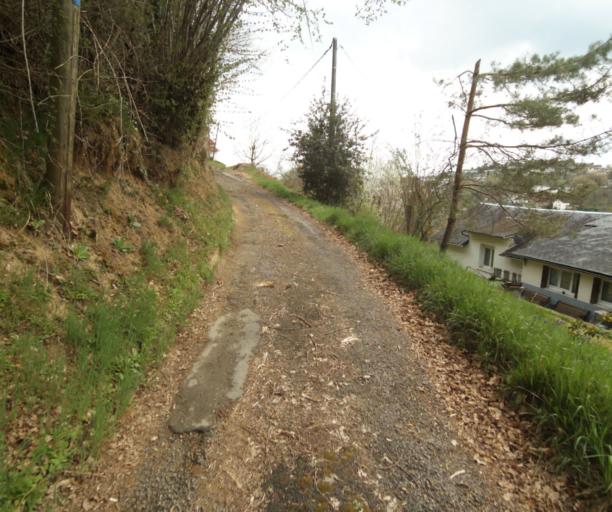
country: FR
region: Limousin
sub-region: Departement de la Correze
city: Tulle
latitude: 45.2634
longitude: 1.7485
